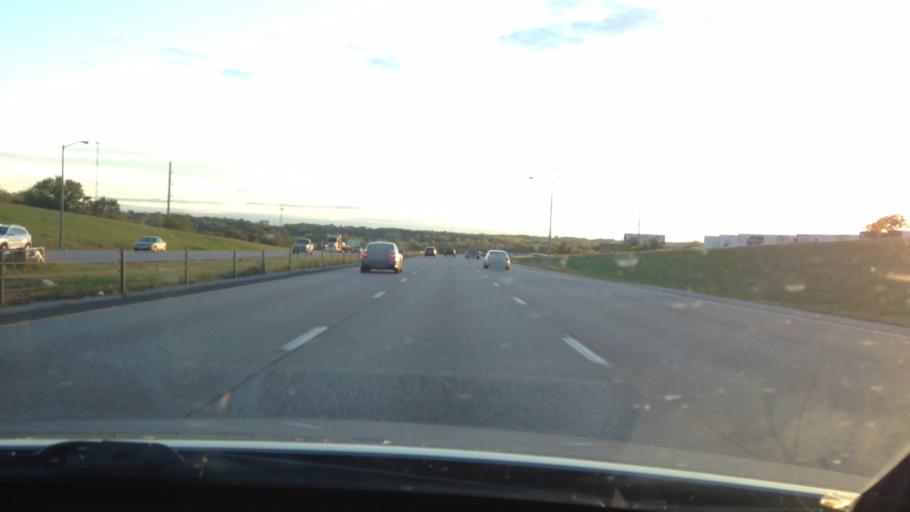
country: US
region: Missouri
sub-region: Jackson County
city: Raytown
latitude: 39.0555
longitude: -94.4943
